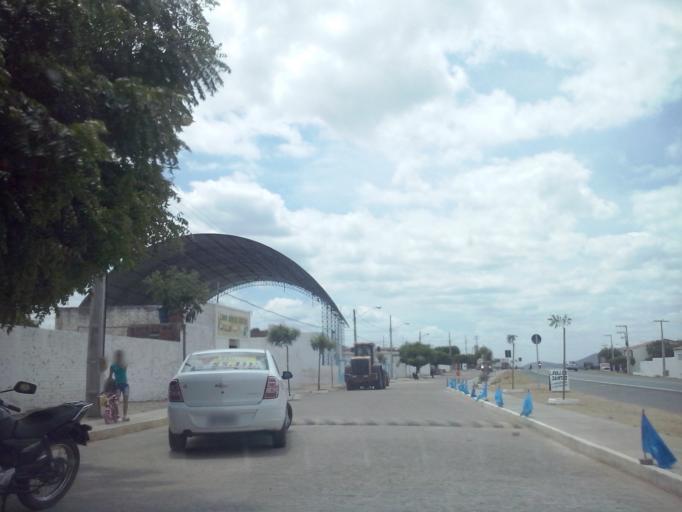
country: BR
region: Paraiba
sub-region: Patos
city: Patos
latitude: -6.9042
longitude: -37.5188
